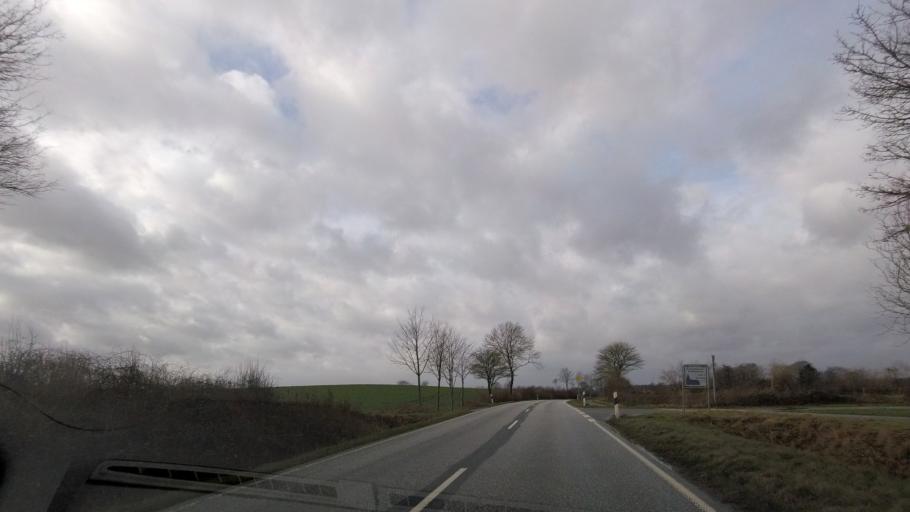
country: DE
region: Schleswig-Holstein
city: Rabenkirchen-Fauluck
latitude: 54.6451
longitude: 9.8559
